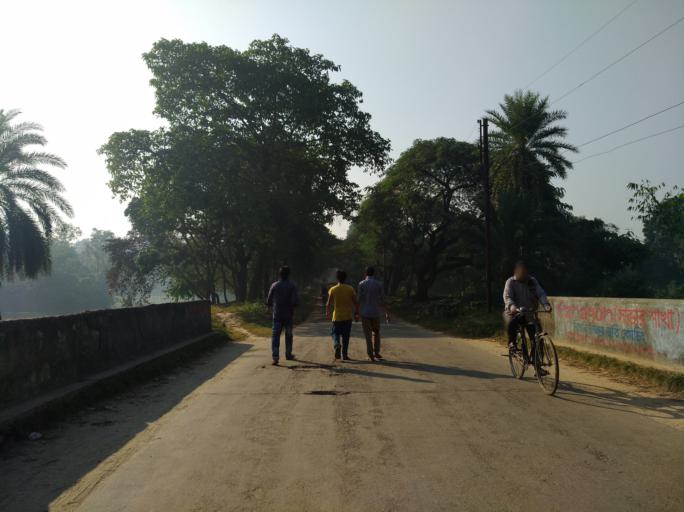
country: BD
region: Dhaka
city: Tungi
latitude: 23.8939
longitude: 90.2679
